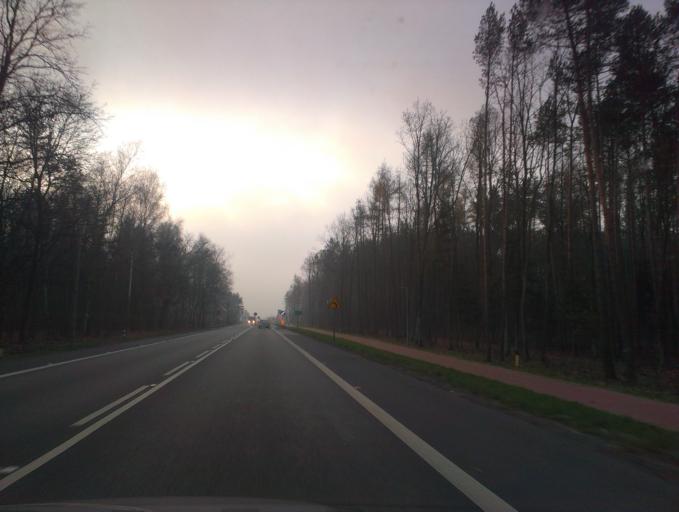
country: PL
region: Greater Poland Voivodeship
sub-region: Powiat chodzieski
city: Chodziez
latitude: 52.9662
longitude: 16.9326
